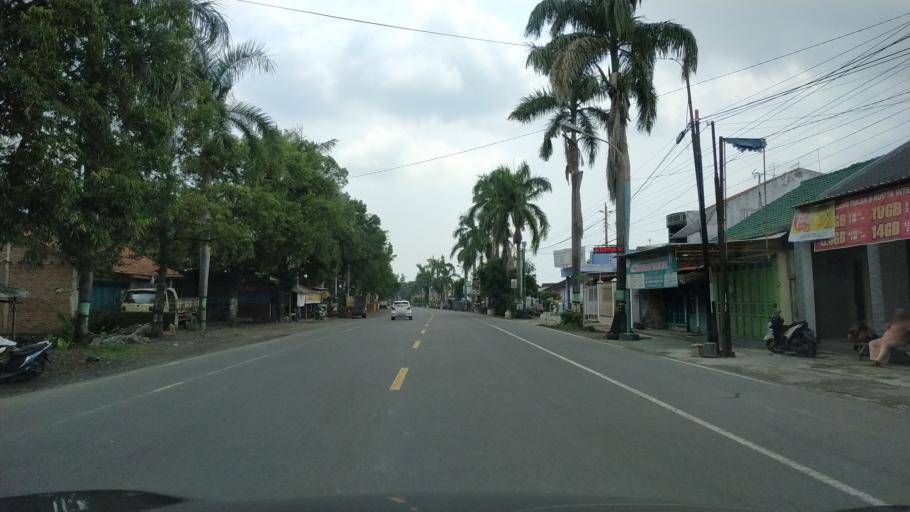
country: ID
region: Central Java
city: Slawi
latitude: -7.0019
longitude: 109.1408
